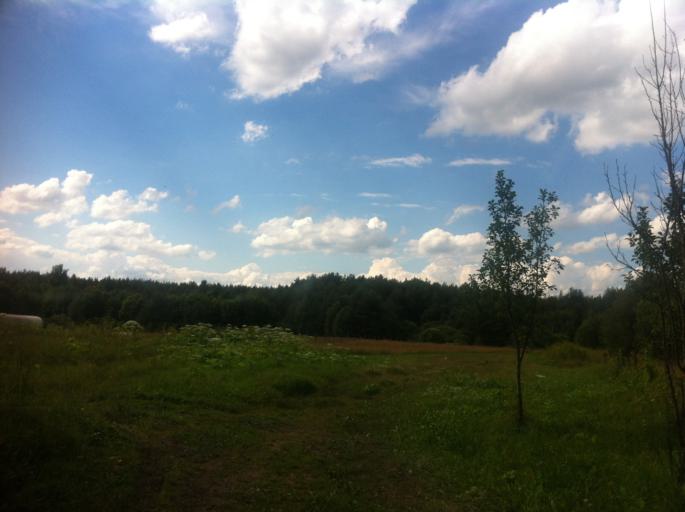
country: RU
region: Pskov
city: Izborsk
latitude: 57.8158
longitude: 27.9507
